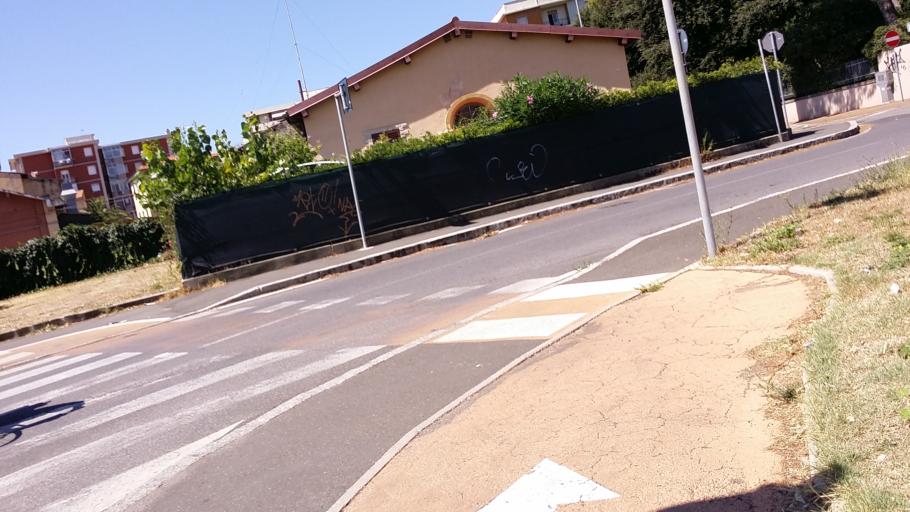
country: IT
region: Tuscany
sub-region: Provincia di Livorno
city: Livorno
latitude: 43.5312
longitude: 10.3156
